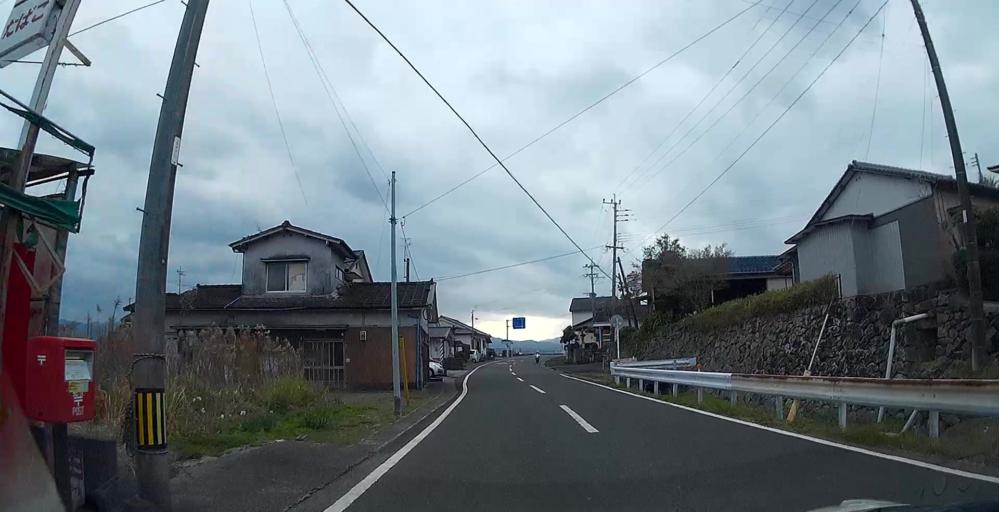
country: JP
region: Kagoshima
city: Izumi
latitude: 32.0934
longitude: 130.2740
